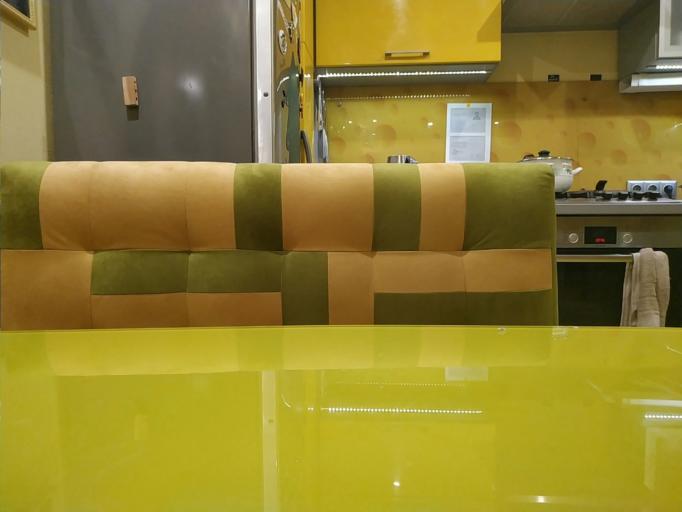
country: RU
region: Murmansk
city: Alakurtti
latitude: 66.2621
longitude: 30.2618
